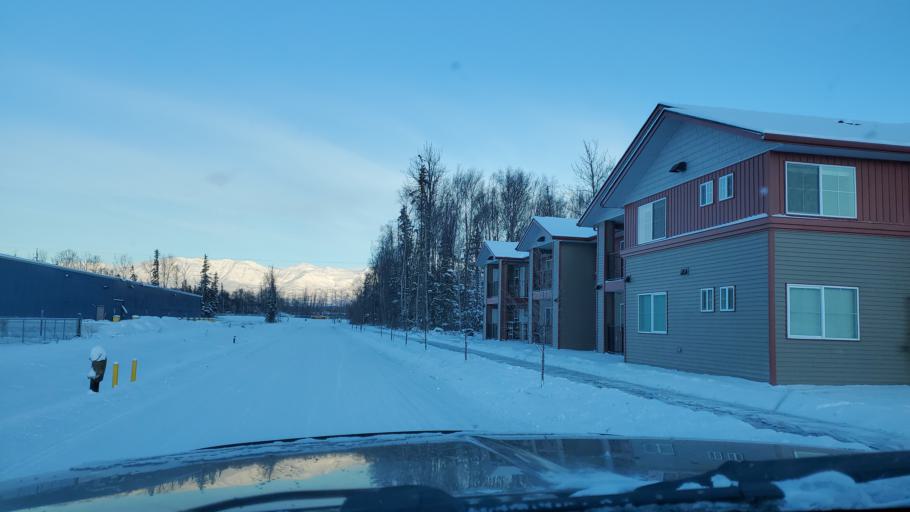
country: US
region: Alaska
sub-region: Matanuska-Susitna Borough
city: Palmer
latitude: 61.5914
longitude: -149.1046
